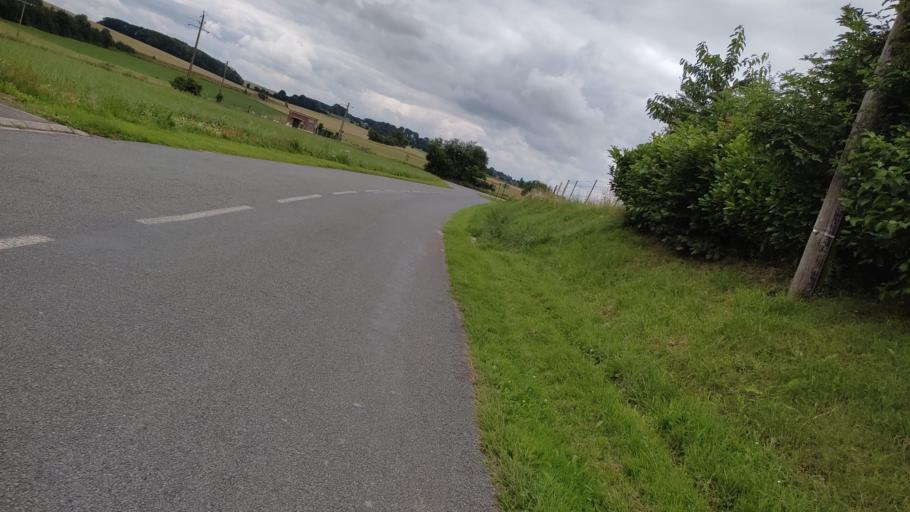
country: FR
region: Nord-Pas-de-Calais
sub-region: Departement du Pas-de-Calais
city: Beaumetz-les-Loges
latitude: 50.2531
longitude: 2.6418
